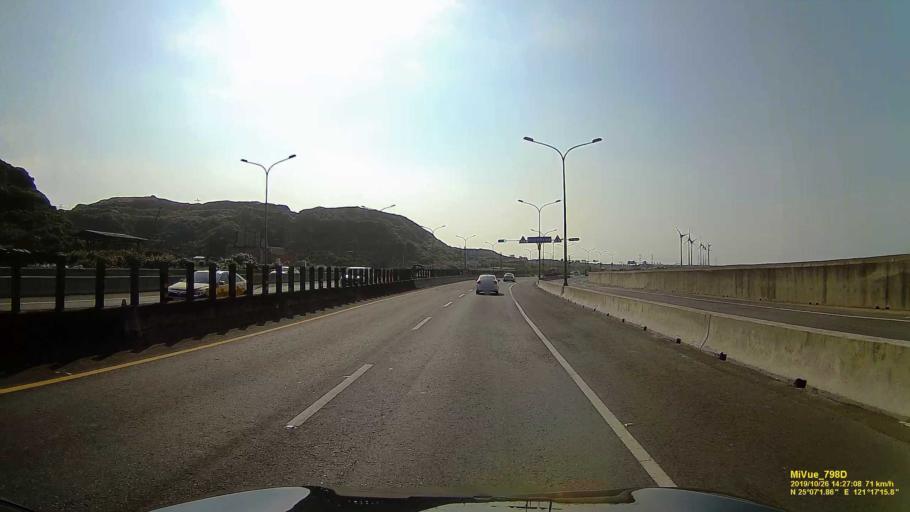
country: TW
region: Taiwan
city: Taoyuan City
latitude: 25.1175
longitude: 121.2882
